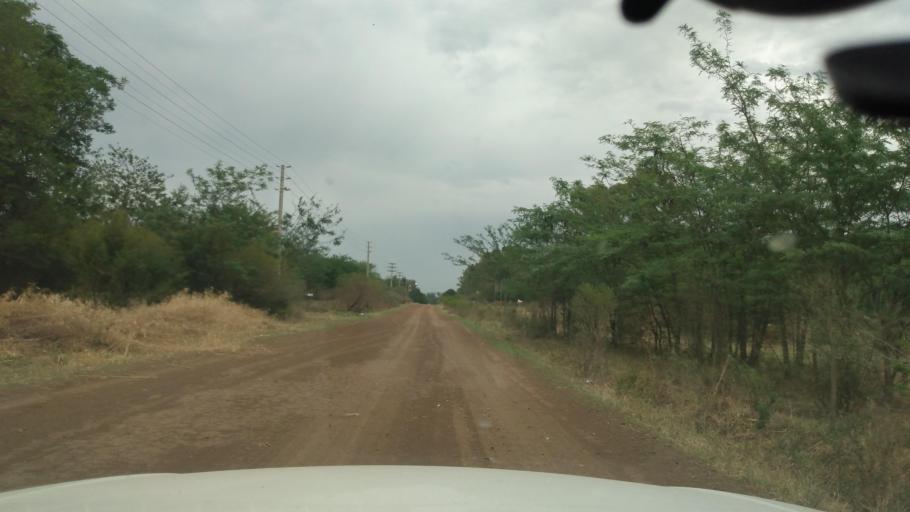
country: AR
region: Buenos Aires
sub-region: Partido de Lujan
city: Lujan
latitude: -34.5580
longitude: -59.1828
